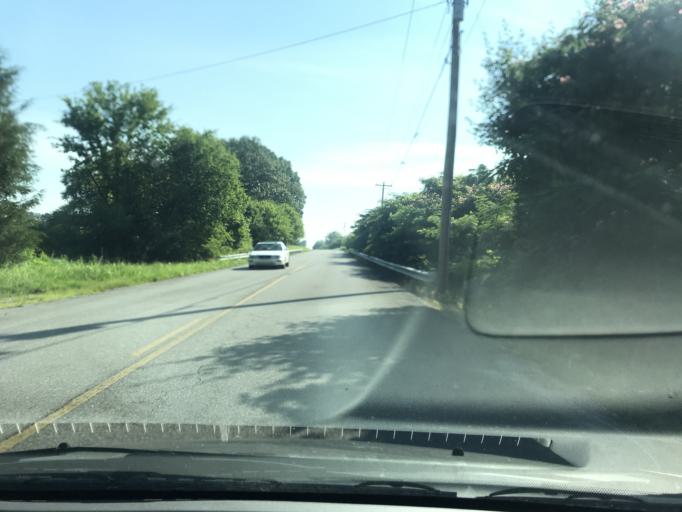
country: US
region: Tennessee
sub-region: Loudon County
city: Loudon
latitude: 35.8104
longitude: -84.3455
